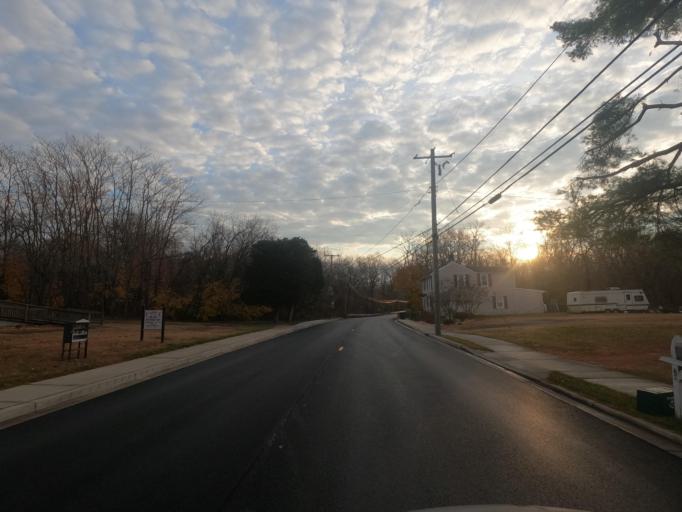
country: US
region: Delaware
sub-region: New Castle County
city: Townsend
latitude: 39.2580
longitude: -75.8339
